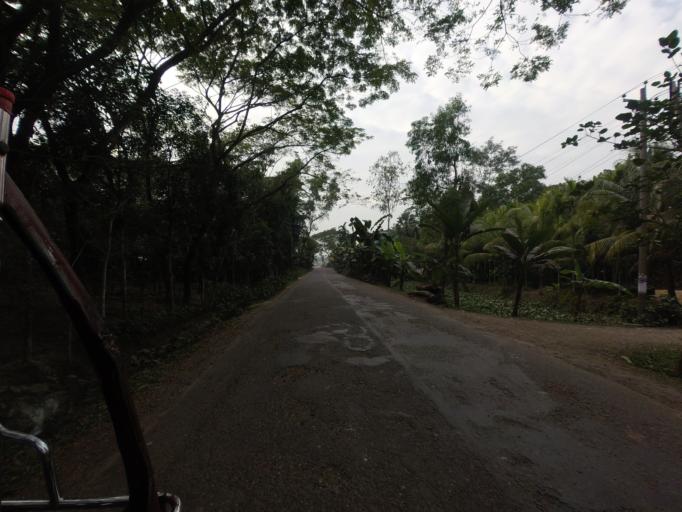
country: BD
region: Barisal
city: Nalchiti
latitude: 22.4544
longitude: 90.3478
